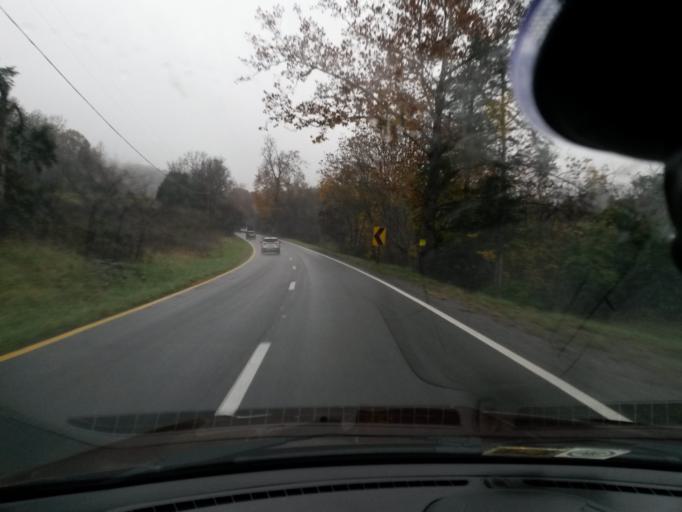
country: US
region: Virginia
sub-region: Botetourt County
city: Fincastle
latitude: 37.5804
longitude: -79.8316
